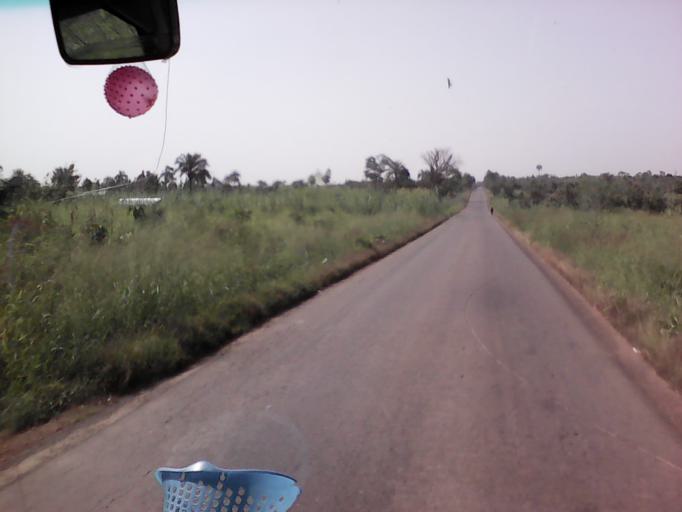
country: TG
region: Centrale
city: Sokode
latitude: 8.8610
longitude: 1.0769
